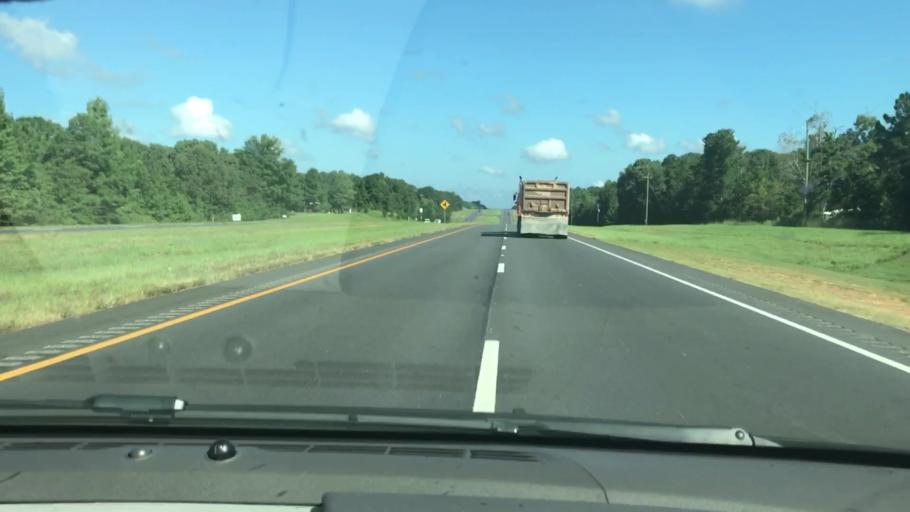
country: US
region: Alabama
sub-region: Barbour County
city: Eufaula
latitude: 32.0308
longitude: -85.1219
